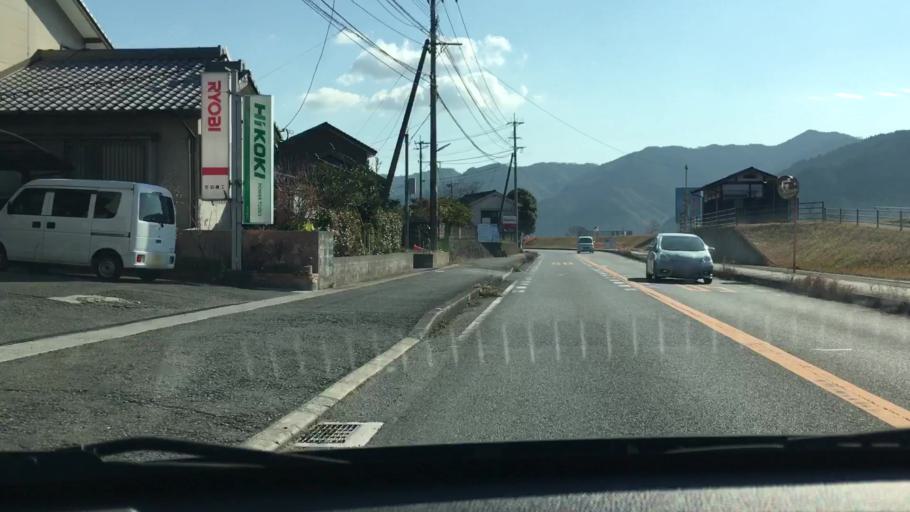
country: JP
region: Oita
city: Saiki
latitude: 32.9606
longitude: 131.8407
